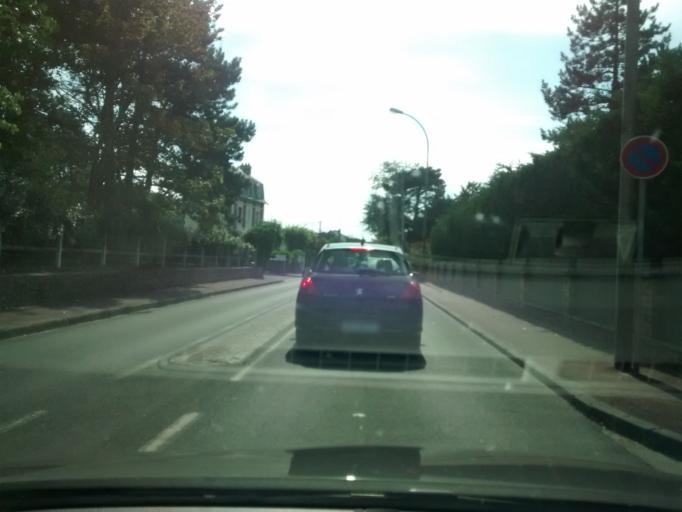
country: FR
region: Lower Normandy
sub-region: Departement du Calvados
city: Deauville
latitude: 49.3500
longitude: 0.0537
